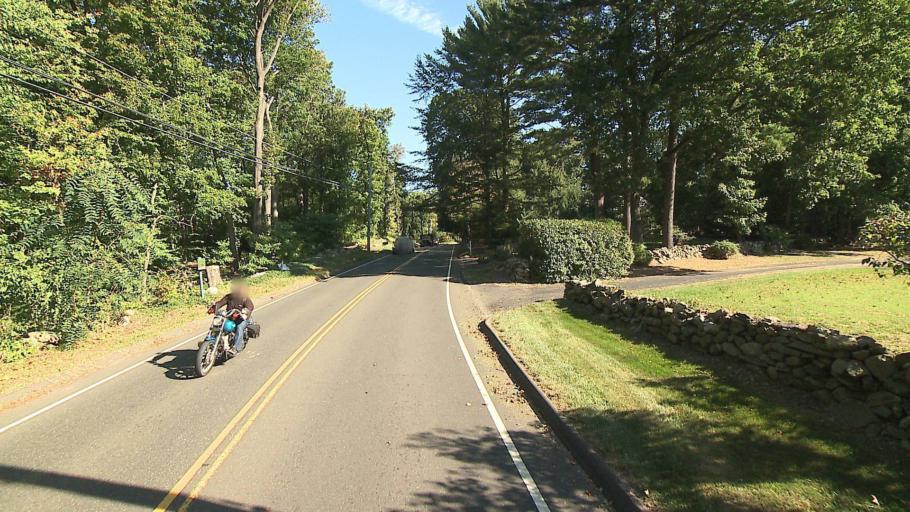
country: US
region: Connecticut
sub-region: Fairfield County
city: New Canaan
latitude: 41.1150
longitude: -73.4857
